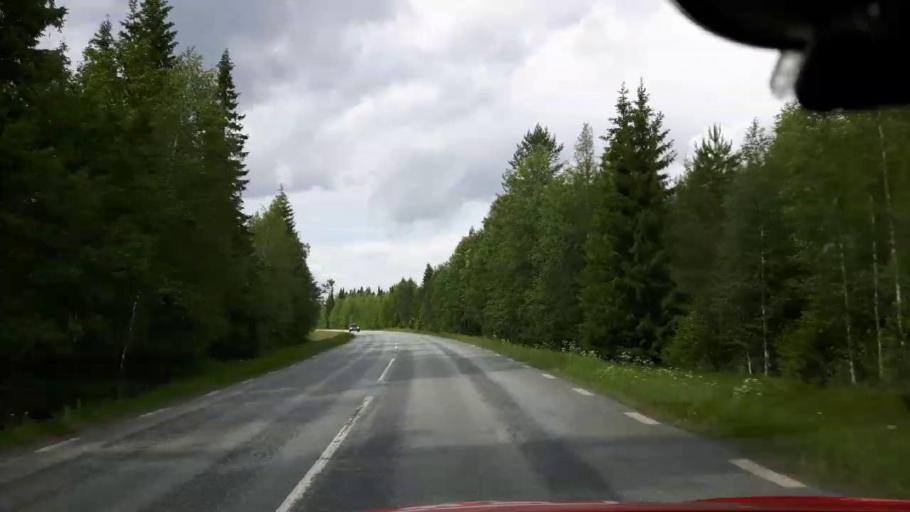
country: SE
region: Jaemtland
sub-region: Krokoms Kommun
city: Krokom
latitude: 63.4031
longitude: 14.3076
